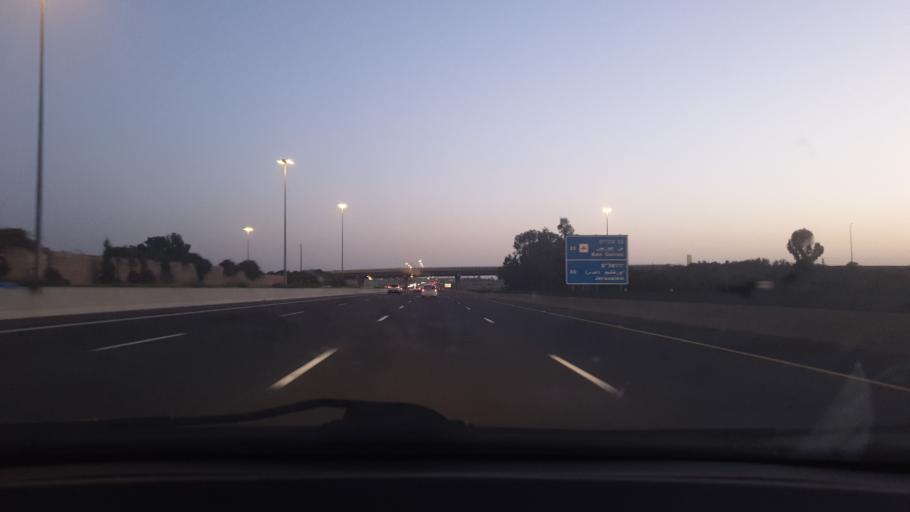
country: IL
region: Central District
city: Rosh Ha'Ayin
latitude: 32.0995
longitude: 34.9354
